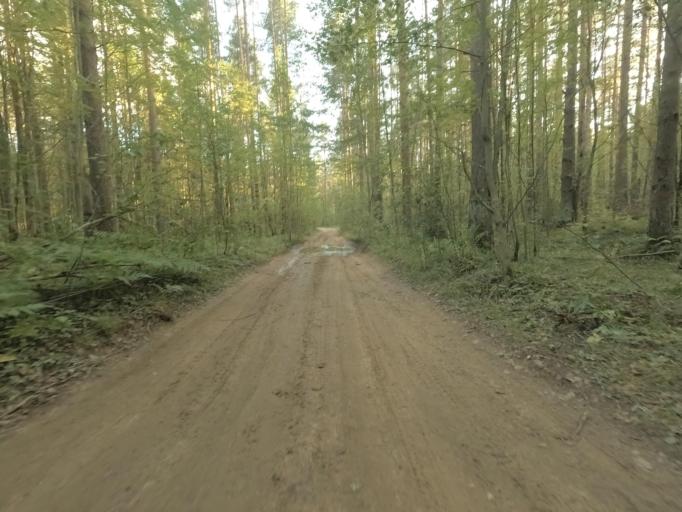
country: RU
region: Leningrad
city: Otradnoye
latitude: 59.8508
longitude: 30.7962
